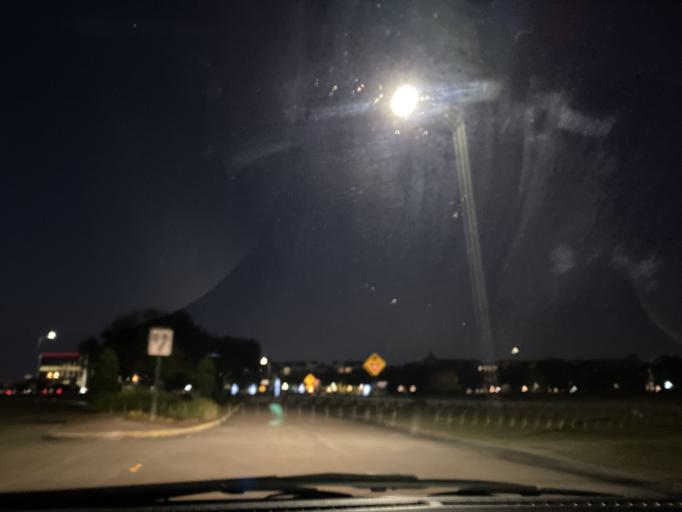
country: US
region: Texas
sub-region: Harris County
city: Bunker Hill Village
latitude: 29.7305
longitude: -95.5543
